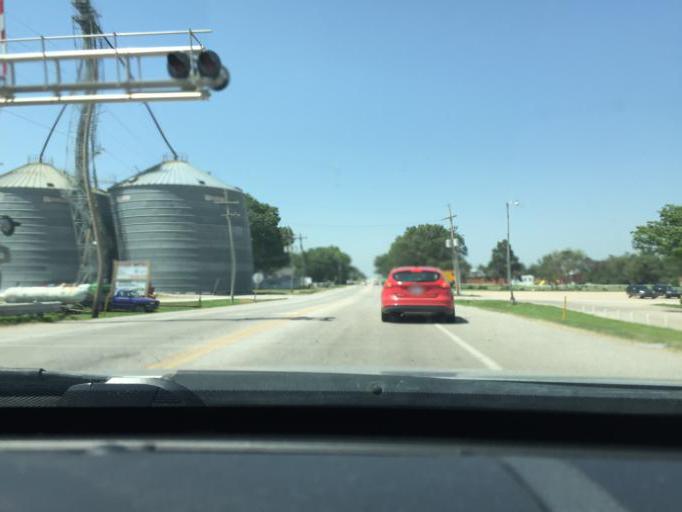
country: US
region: Kansas
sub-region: Reno County
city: Haven
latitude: 37.9384
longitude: -97.8667
